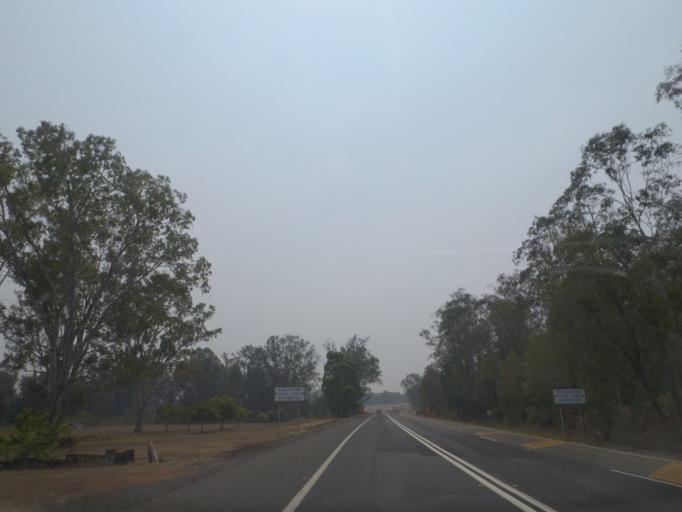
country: AU
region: New South Wales
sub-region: Clarence Valley
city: Maclean
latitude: -29.5530
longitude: 153.1534
